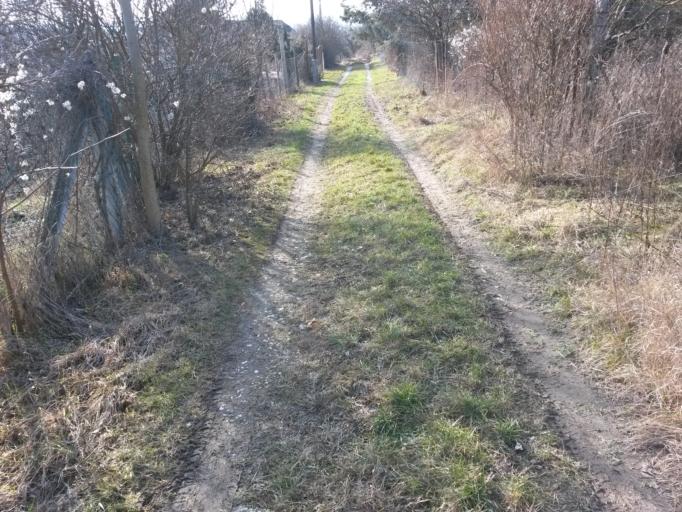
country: HU
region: Pest
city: Zsambek
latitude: 47.5500
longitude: 18.7070
